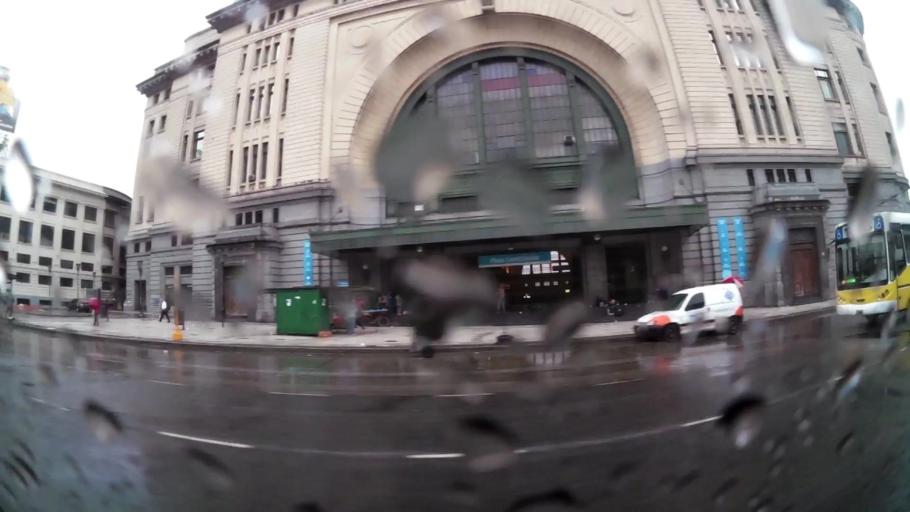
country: AR
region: Buenos Aires F.D.
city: Buenos Aires
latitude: -34.6283
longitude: -58.3792
